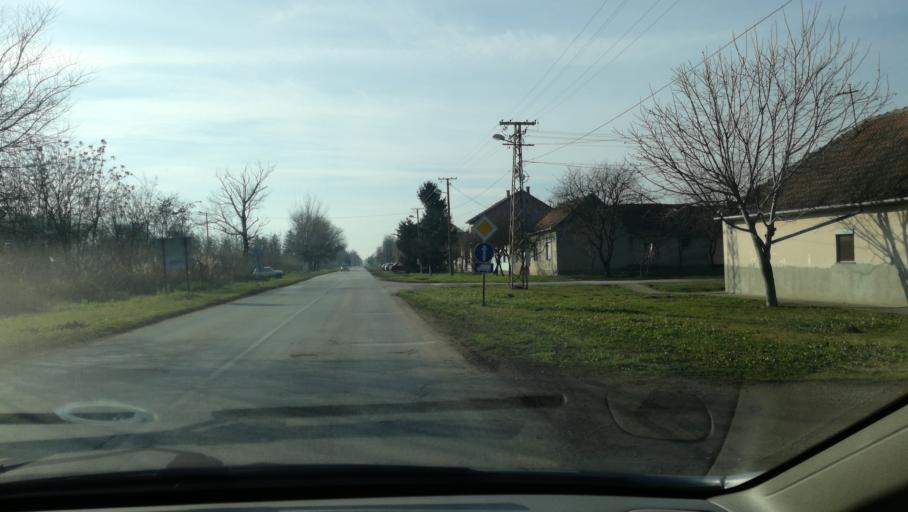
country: RS
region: Autonomna Pokrajina Vojvodina
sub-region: Severnobanatski Okrug
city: Kikinda
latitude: 45.8323
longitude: 20.4902
